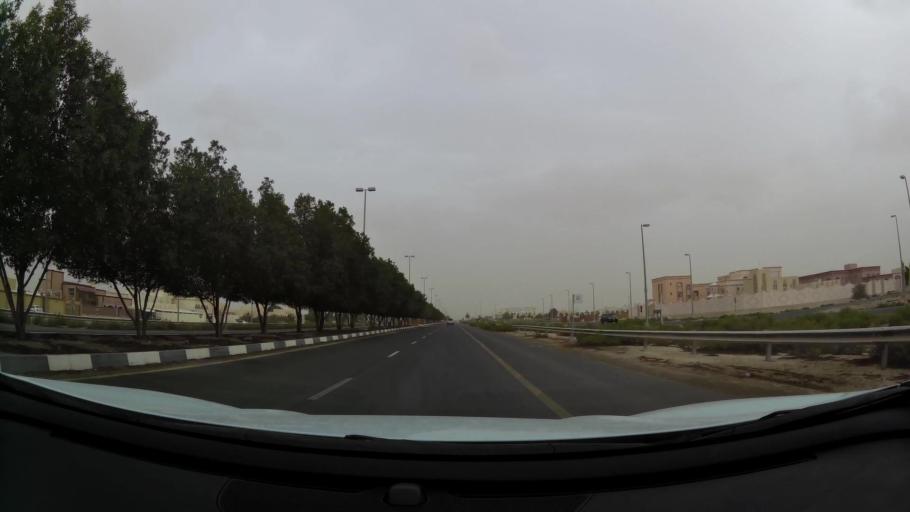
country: AE
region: Abu Dhabi
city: Abu Dhabi
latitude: 24.3821
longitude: 54.6962
